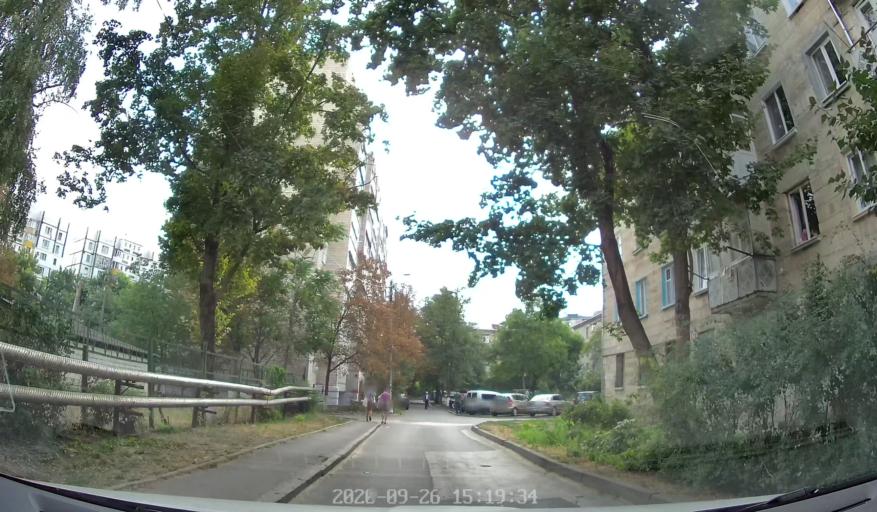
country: MD
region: Chisinau
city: Chisinau
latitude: 47.0214
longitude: 28.8091
